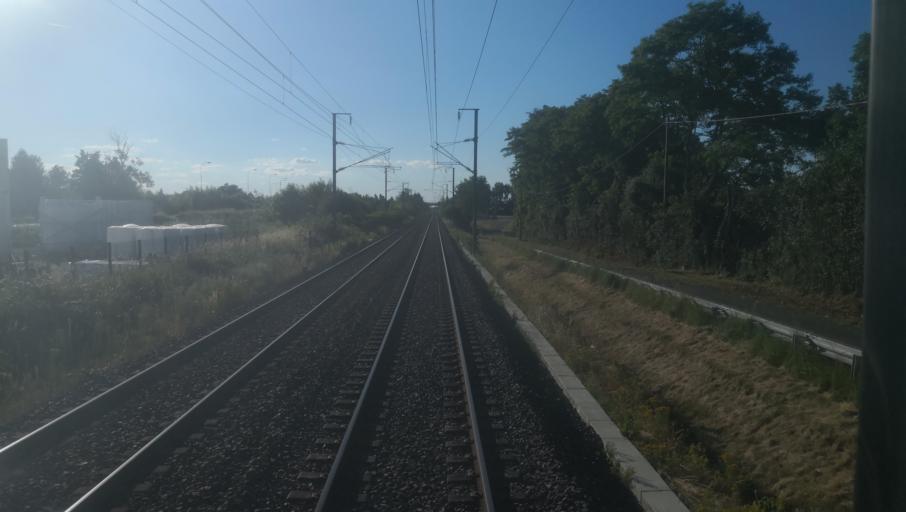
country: FR
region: Auvergne
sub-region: Departement de l'Allier
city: Avermes
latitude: 46.5938
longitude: 3.3121
